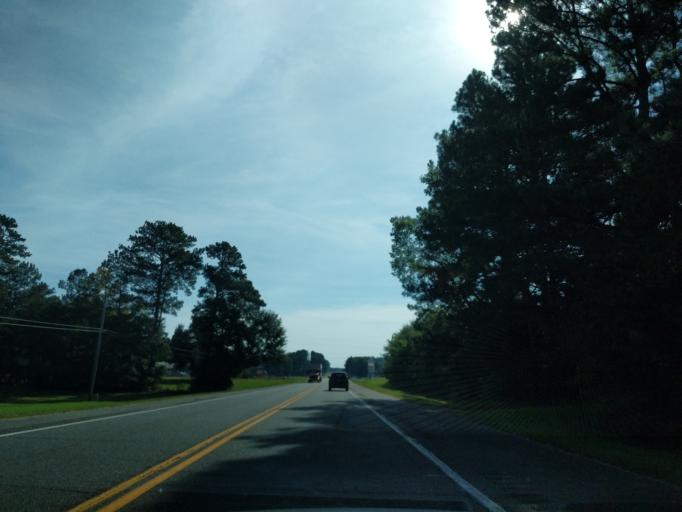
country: US
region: Georgia
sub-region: Troup County
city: Hogansville
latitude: 33.1623
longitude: -84.8770
